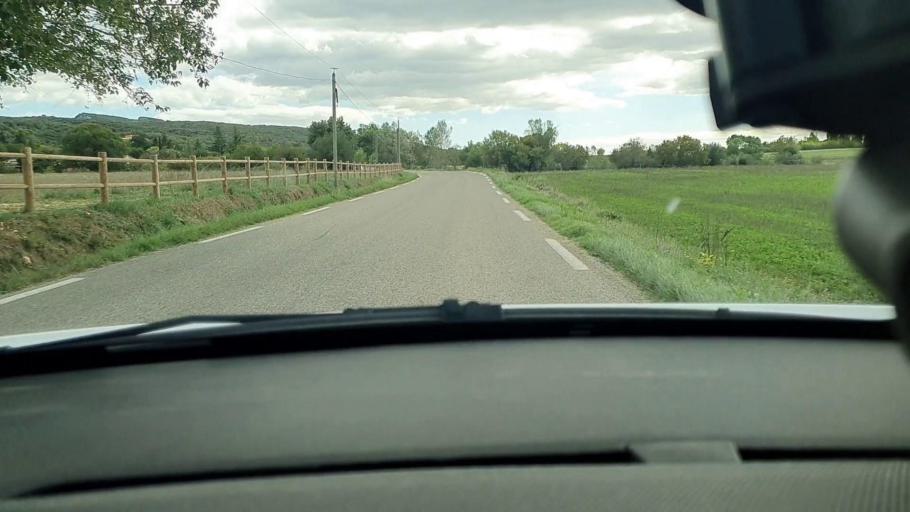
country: FR
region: Languedoc-Roussillon
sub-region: Departement du Gard
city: Salindres
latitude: 44.1813
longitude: 4.2356
